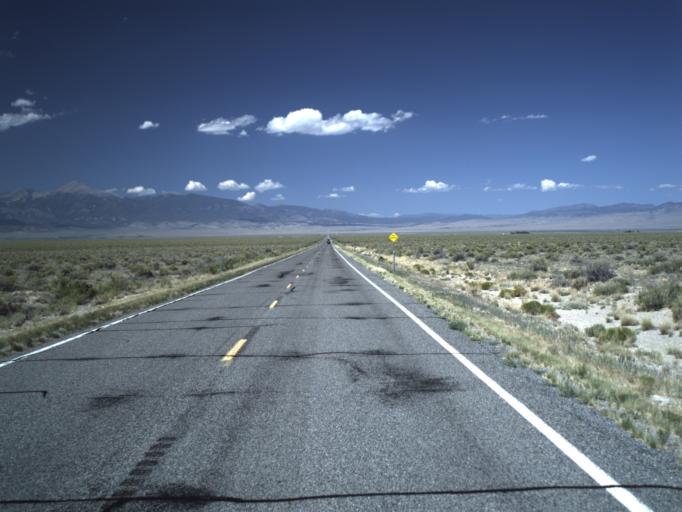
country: US
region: Nevada
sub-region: White Pine County
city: McGill
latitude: 39.0447
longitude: -113.8866
